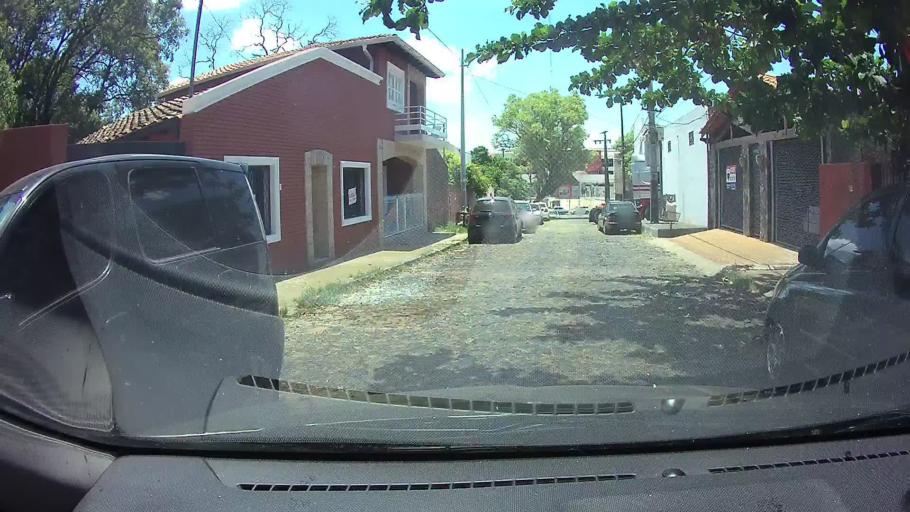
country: PY
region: Central
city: Lambare
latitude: -25.3103
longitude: -57.5941
